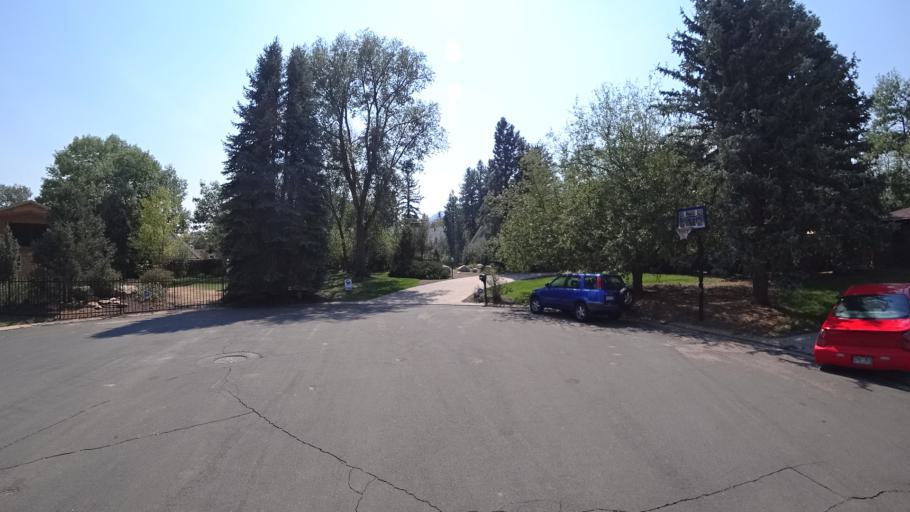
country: US
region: Colorado
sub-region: El Paso County
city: Colorado Springs
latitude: 38.7961
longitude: -104.8370
